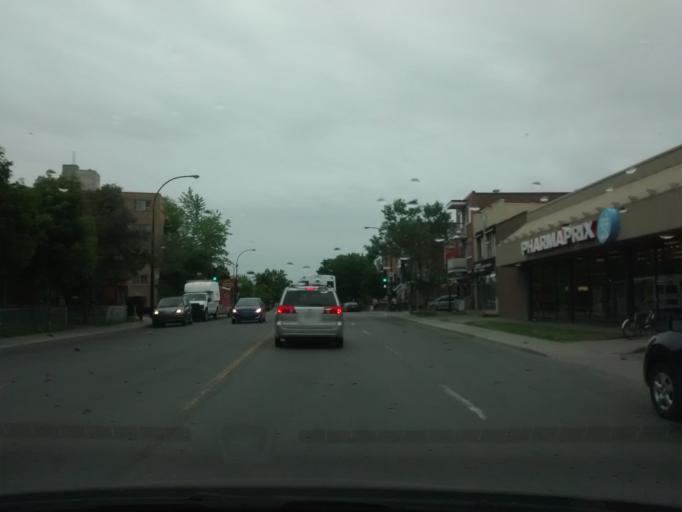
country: CA
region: Quebec
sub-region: Montreal
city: Montreal
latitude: 45.5485
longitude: -73.5847
